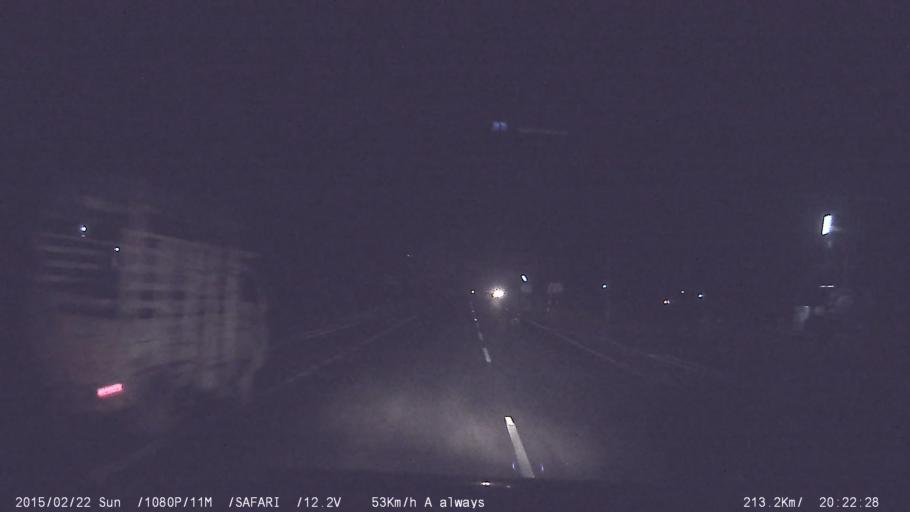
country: IN
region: Tamil Nadu
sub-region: Dindigul
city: Dindigul
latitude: 10.2954
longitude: 77.8814
